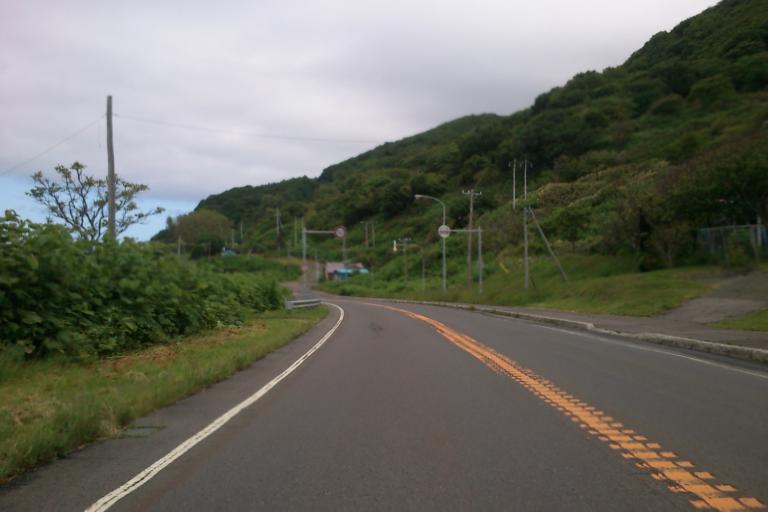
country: JP
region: Hokkaido
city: Ishikari
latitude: 43.4207
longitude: 141.4293
